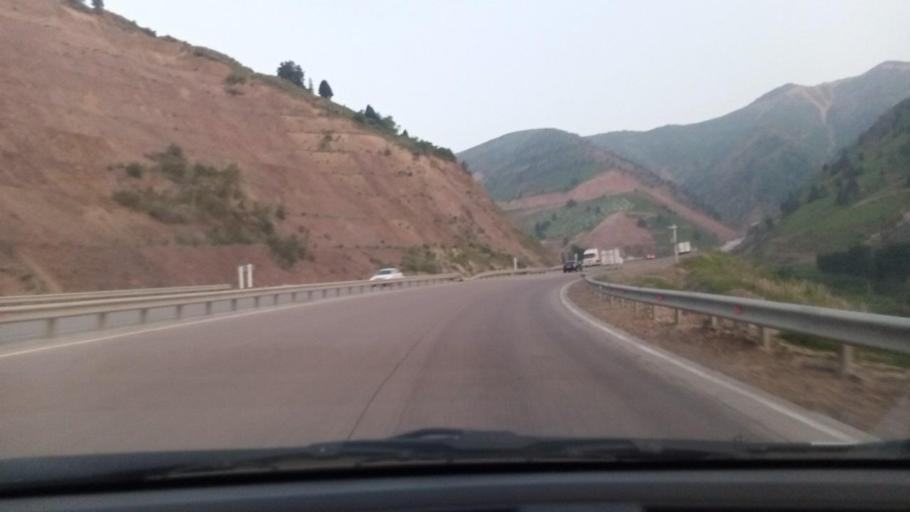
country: UZ
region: Toshkent
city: Angren
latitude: 41.1150
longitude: 70.4967
